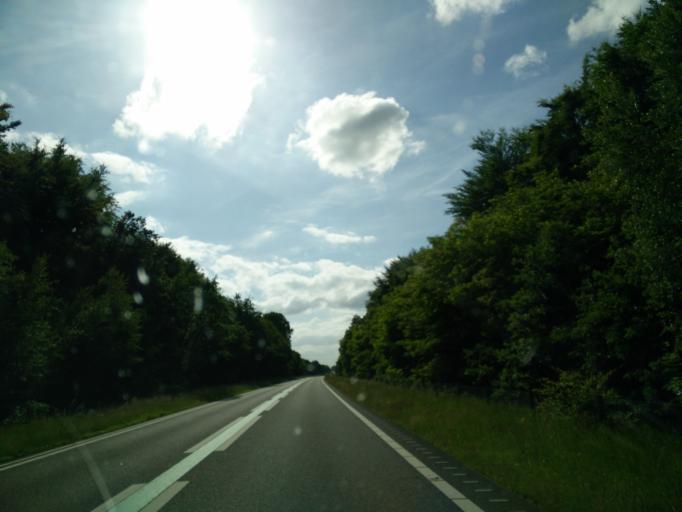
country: NL
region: Drenthe
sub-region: Gemeente Coevorden
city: Sleen
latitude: 52.8005
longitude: 6.7587
